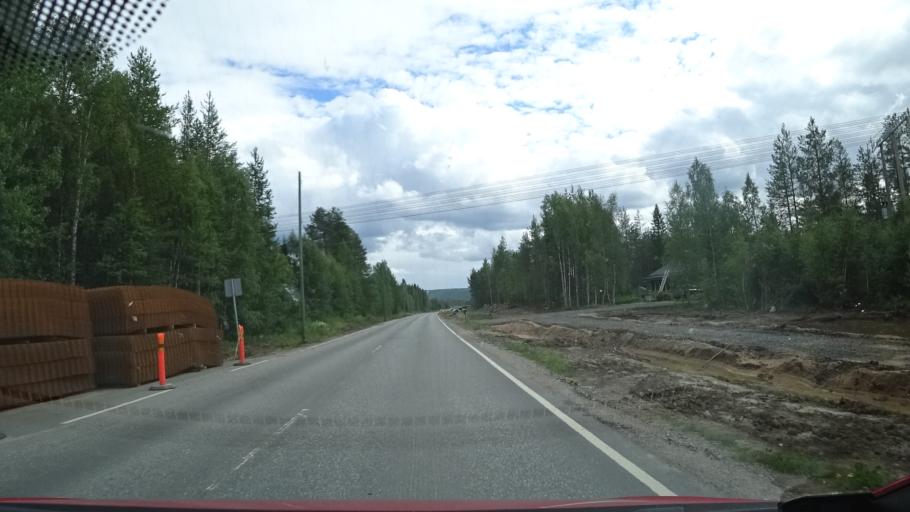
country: FI
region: Lapland
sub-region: Rovaniemi
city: Rovaniemi
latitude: 66.5339
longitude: 25.7317
